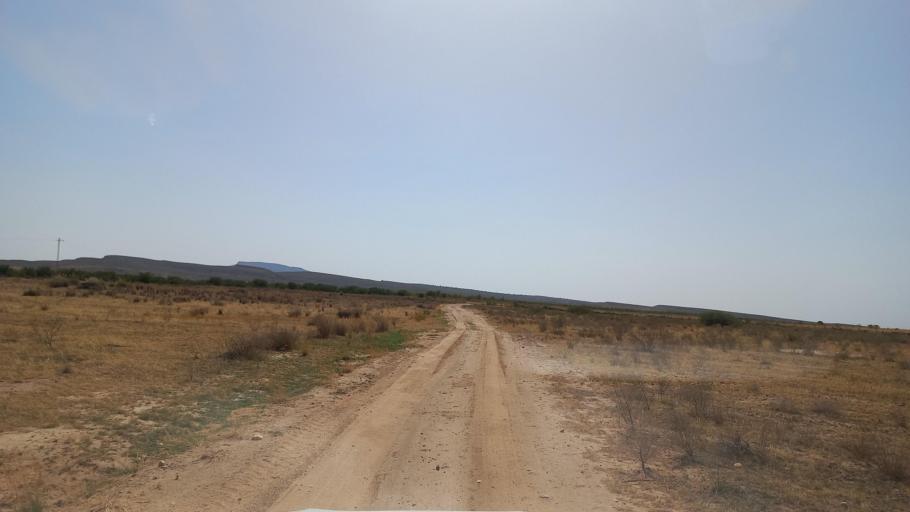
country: TN
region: Al Qasrayn
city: Kasserine
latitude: 35.2153
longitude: 9.0317
